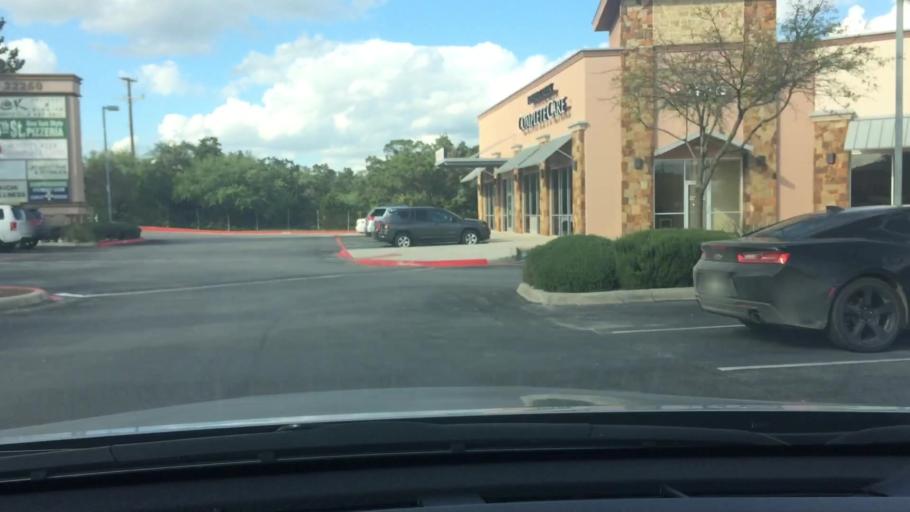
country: US
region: Texas
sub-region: Bexar County
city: Timberwood Park
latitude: 29.6488
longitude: -98.4256
